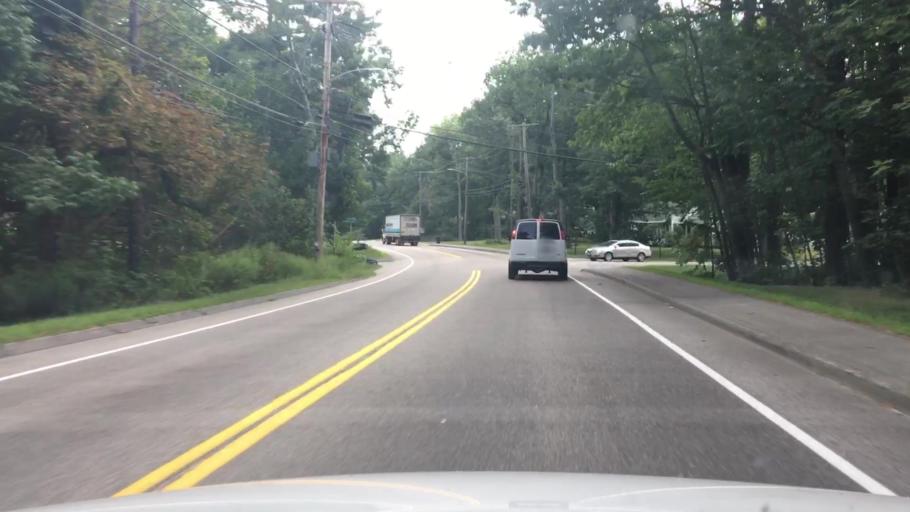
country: US
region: Maine
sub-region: Cumberland County
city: Falmouth
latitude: 43.7265
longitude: -70.2486
